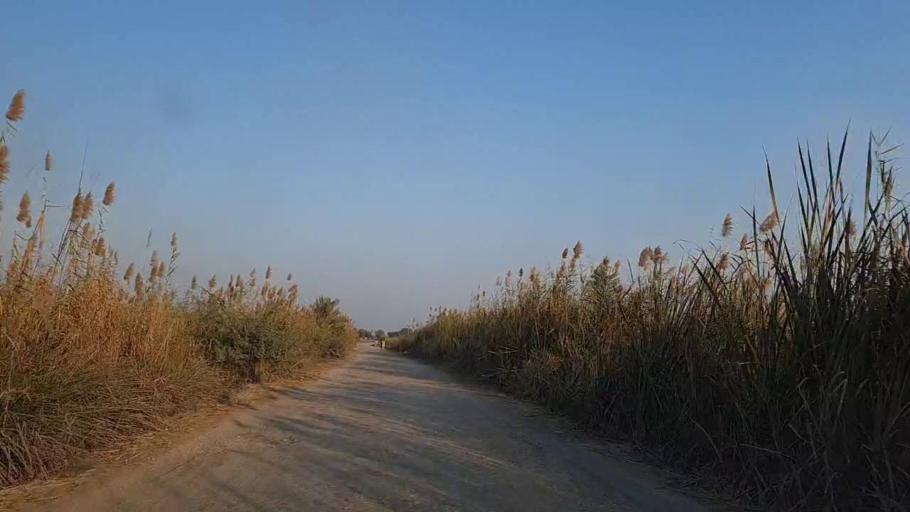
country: PK
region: Sindh
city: Daur
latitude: 26.5105
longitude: 68.3021
